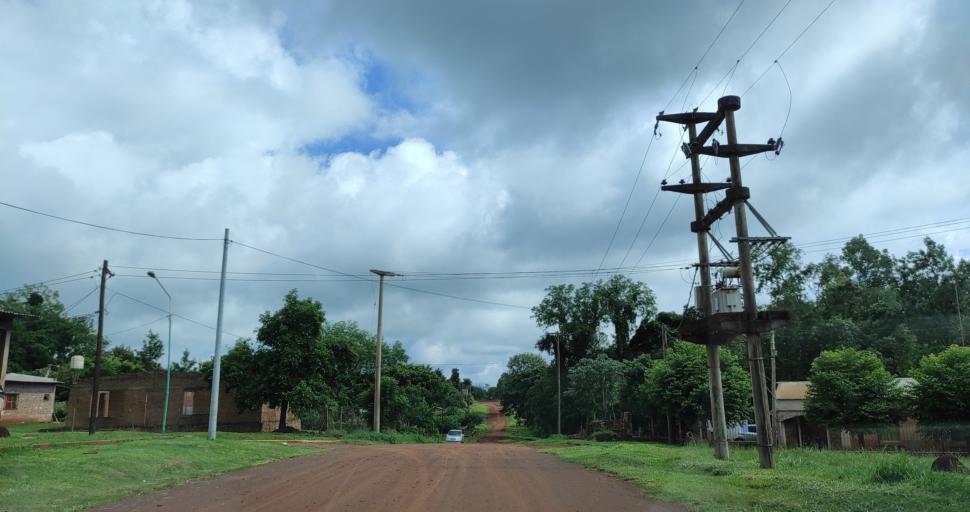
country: AR
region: Corrientes
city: San Carlos
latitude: -27.7431
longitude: -55.8956
